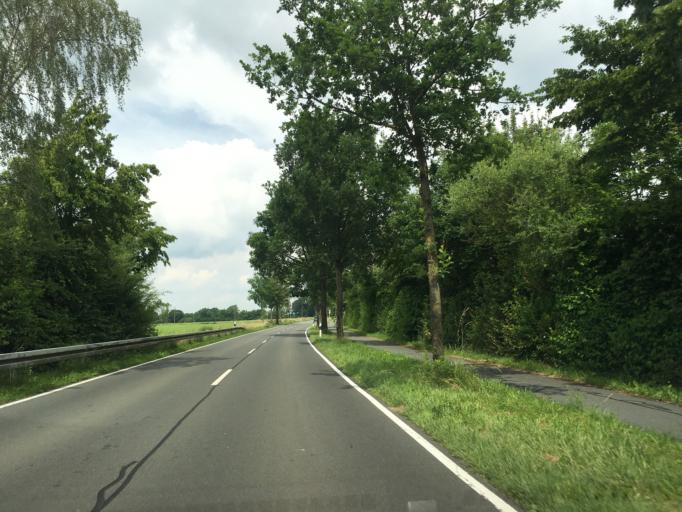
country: DE
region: North Rhine-Westphalia
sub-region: Regierungsbezirk Munster
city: Altenberge
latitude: 51.9903
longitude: 7.5341
